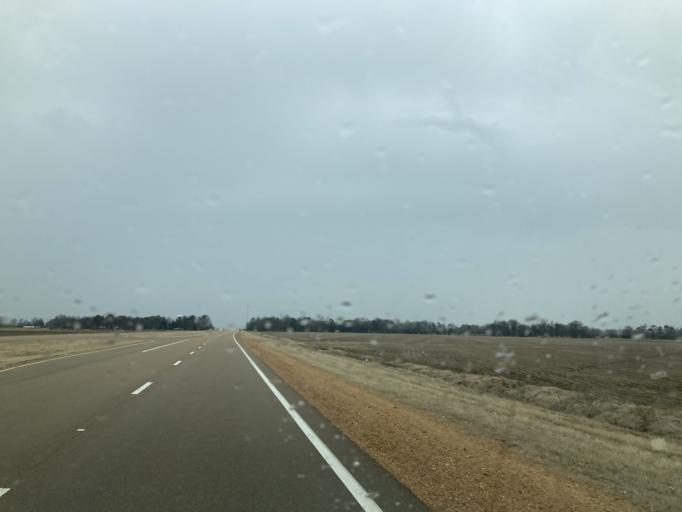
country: US
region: Mississippi
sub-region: Humphreys County
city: Belzoni
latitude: 33.0859
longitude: -90.4866
